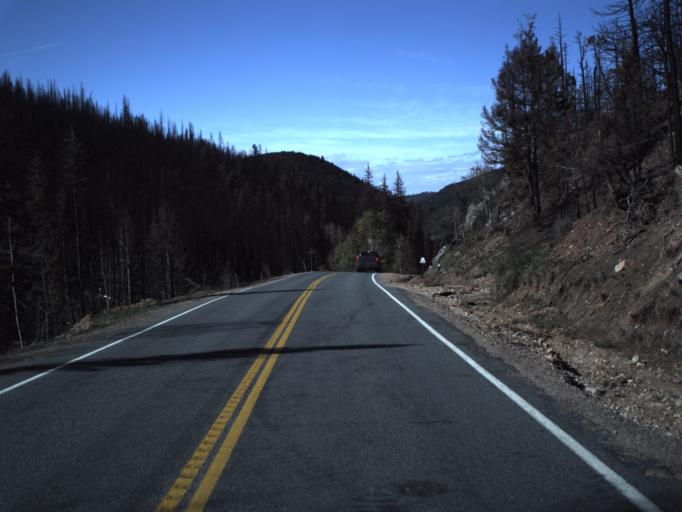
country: US
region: Utah
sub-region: Iron County
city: Parowan
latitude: 37.7381
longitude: -112.8379
